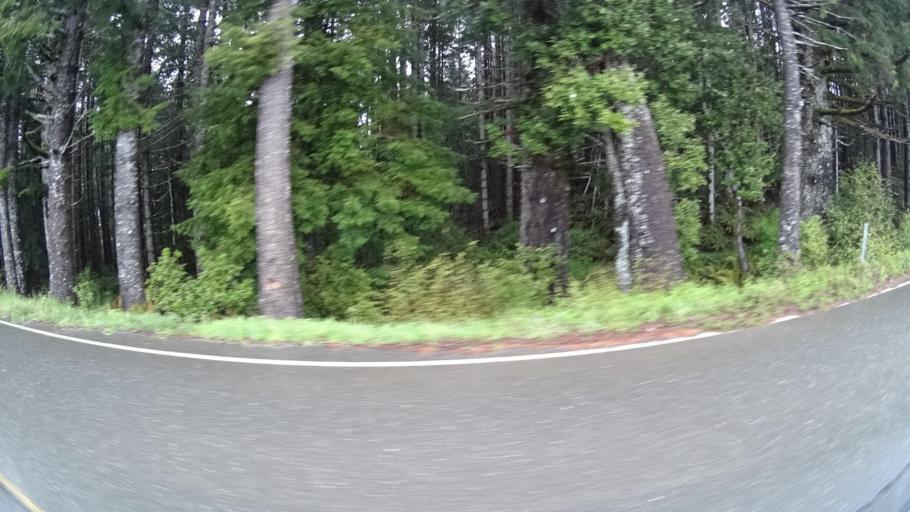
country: US
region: California
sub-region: Humboldt County
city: Westhaven-Moonstone
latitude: 41.1889
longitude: -123.9309
